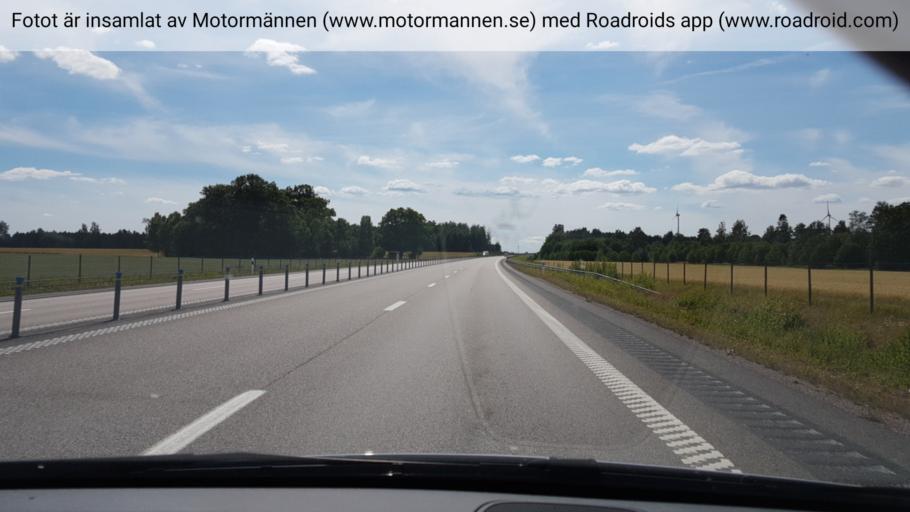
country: SE
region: Vaestra Goetaland
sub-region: Gotene Kommun
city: Goetene
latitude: 58.4992
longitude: 13.5006
